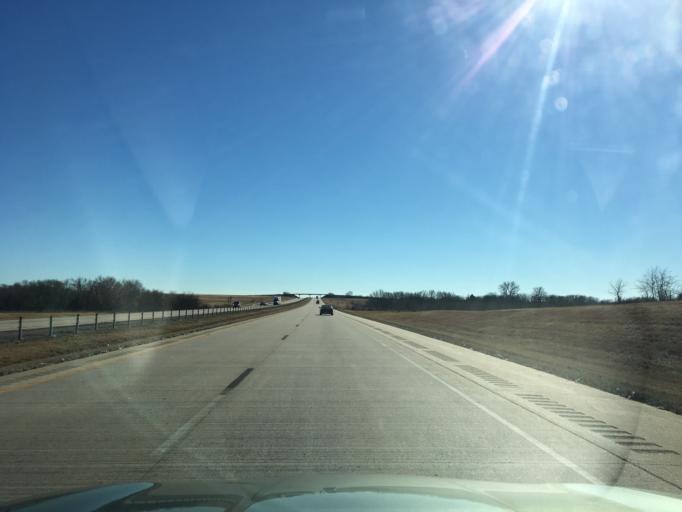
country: US
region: Oklahoma
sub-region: Kay County
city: Tonkawa
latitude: 36.5007
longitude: -97.3345
